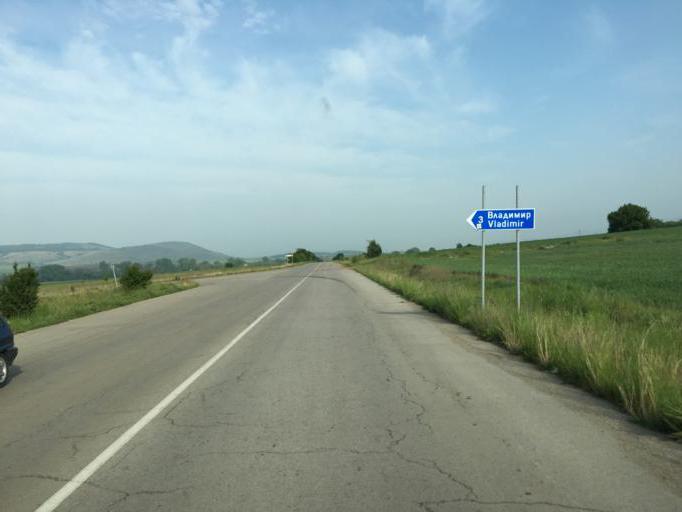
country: BG
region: Kyustendil
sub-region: Obshtina Bobovdol
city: Bobovdol
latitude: 42.4657
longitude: 23.0813
